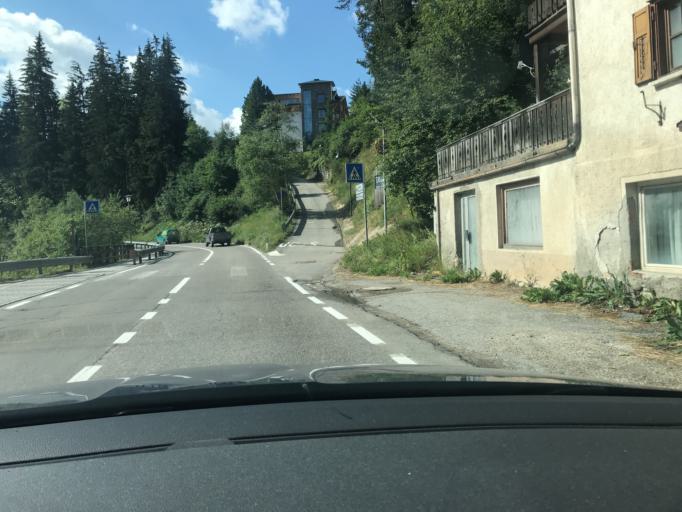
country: IT
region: Trentino-Alto Adige
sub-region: Bolzano
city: Badia
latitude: 46.6085
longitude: 11.8941
